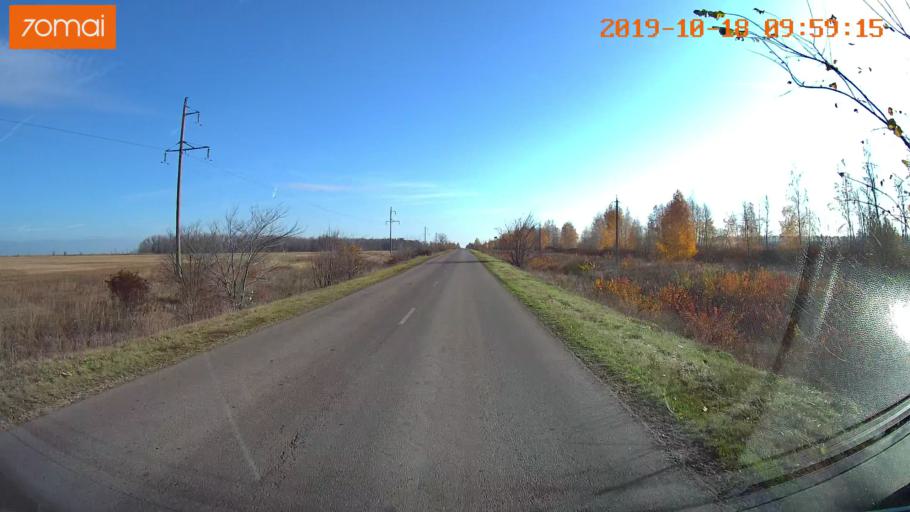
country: RU
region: Tula
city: Kurkino
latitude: 53.3770
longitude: 38.4588
